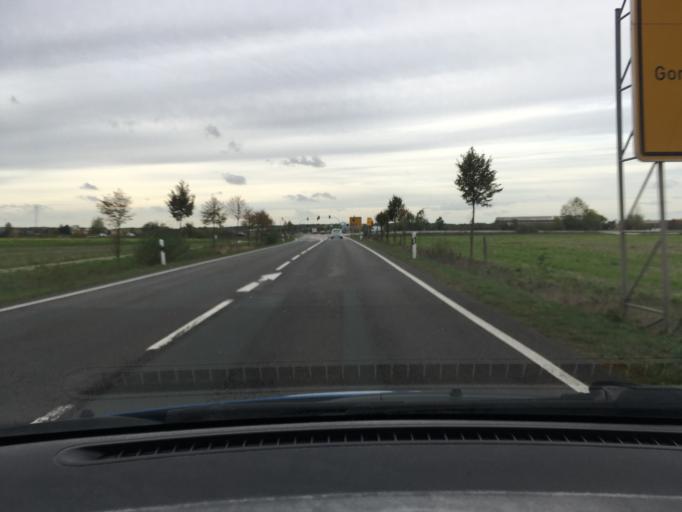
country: DE
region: Saxony-Anhalt
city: Gommern
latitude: 52.0815
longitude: 11.8419
